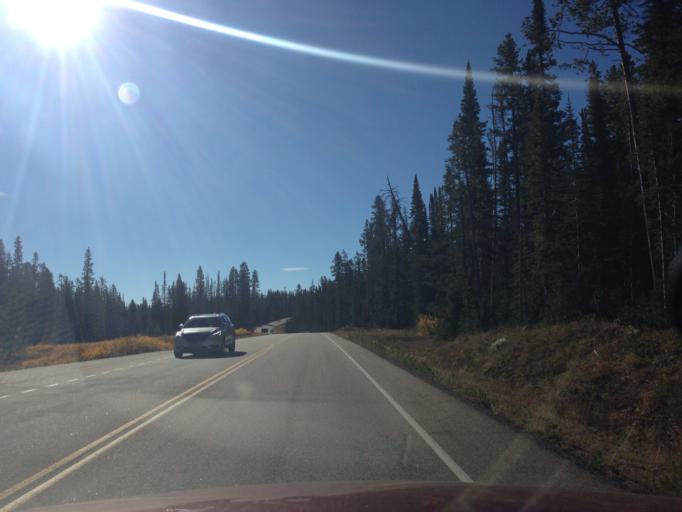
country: US
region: Montana
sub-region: Carbon County
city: Red Lodge
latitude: 45.0199
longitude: -109.8741
